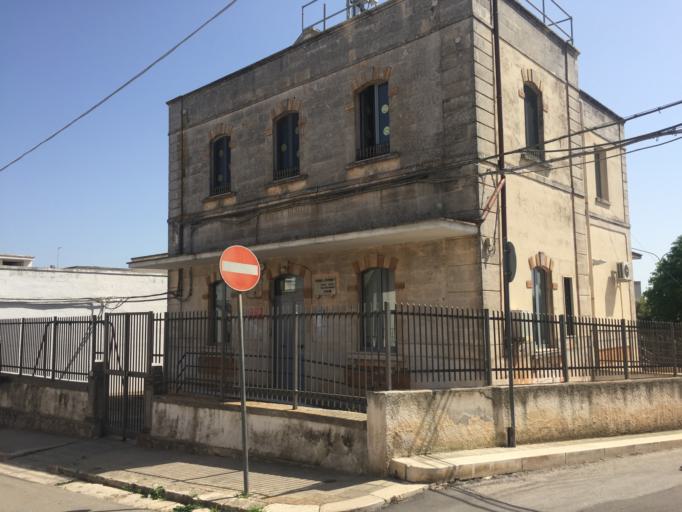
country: IT
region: Apulia
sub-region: Provincia di Brindisi
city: Casalini
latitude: 40.7372
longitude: 17.4712
